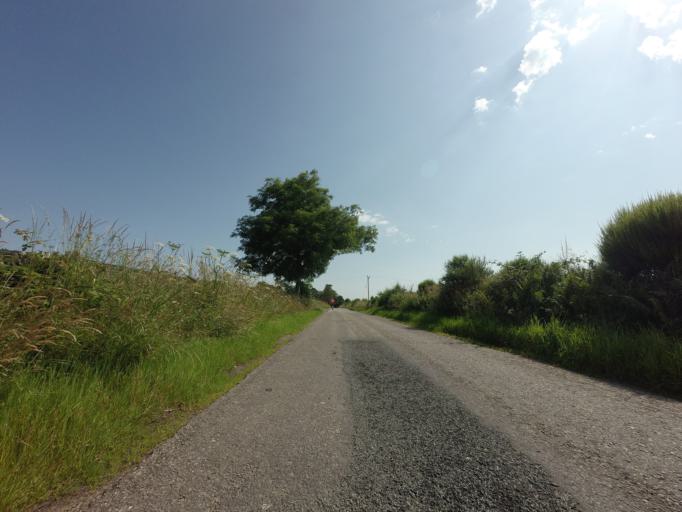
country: GB
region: Scotland
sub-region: Highland
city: Invergordon
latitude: 57.7543
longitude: -4.1517
